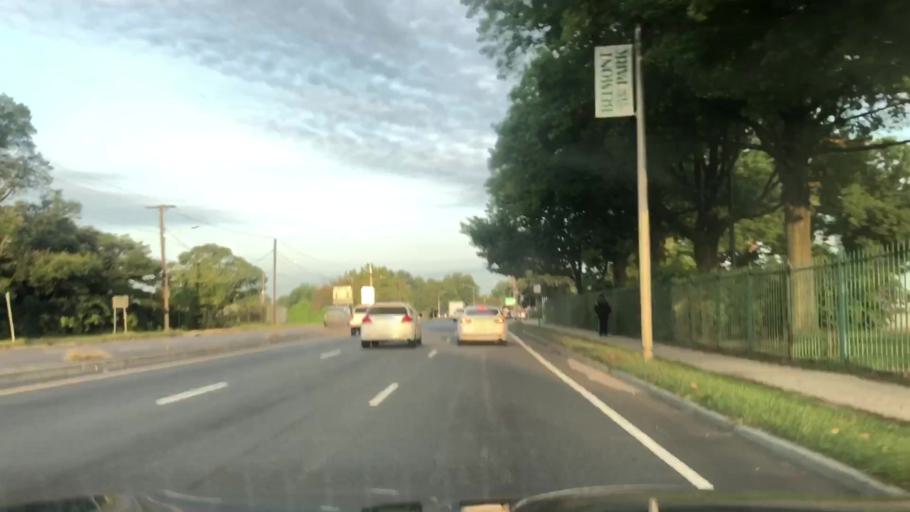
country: US
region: New York
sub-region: Nassau County
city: Bellerose Terrace
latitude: 40.7101
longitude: -73.7247
